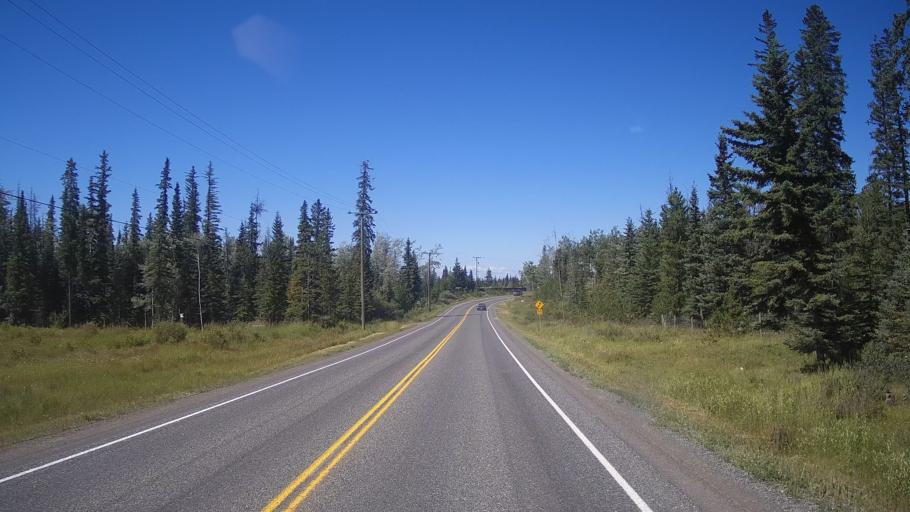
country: CA
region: British Columbia
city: Cache Creek
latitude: 51.5520
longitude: -121.2275
